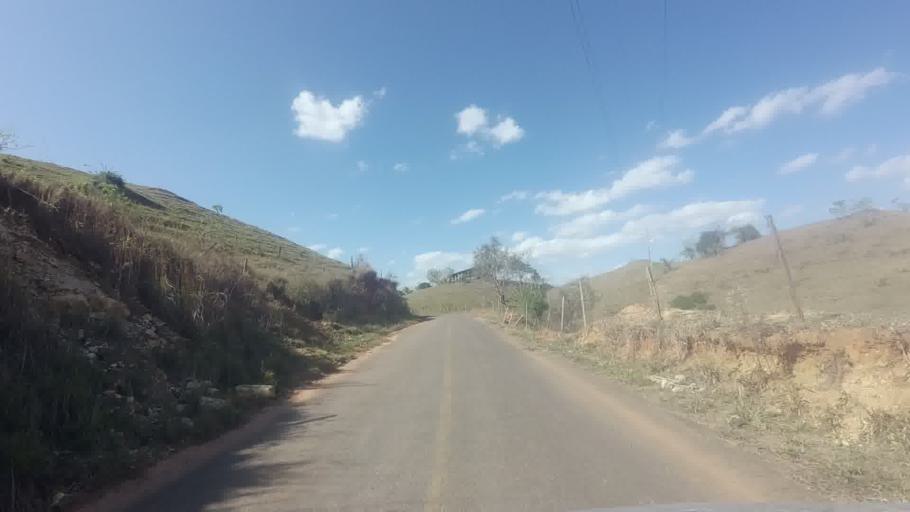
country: BR
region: Rio de Janeiro
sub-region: Bom Jesus Do Itabapoana
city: Bom Jesus do Itabapoana
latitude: -21.1186
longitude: -41.6535
